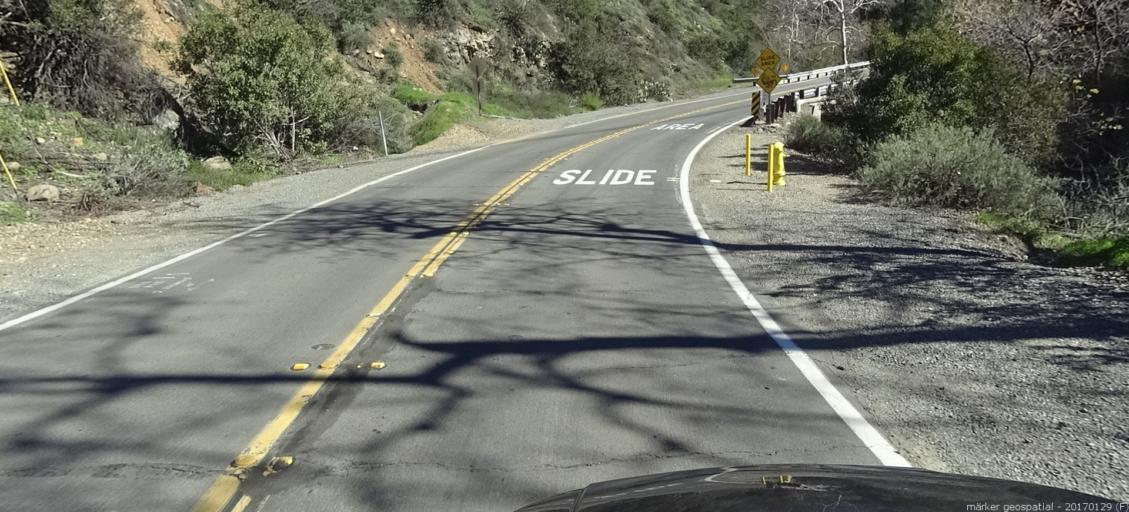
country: US
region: California
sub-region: Orange County
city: Foothill Ranch
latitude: 33.7472
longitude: -117.6329
